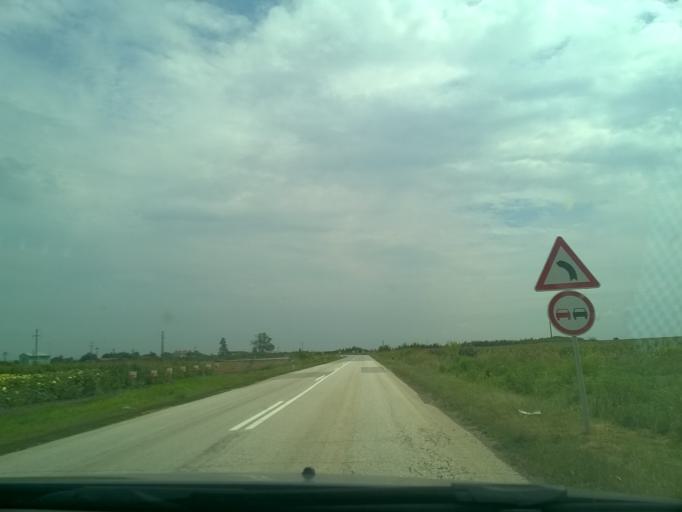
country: RS
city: Boka
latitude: 45.3458
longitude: 20.8199
